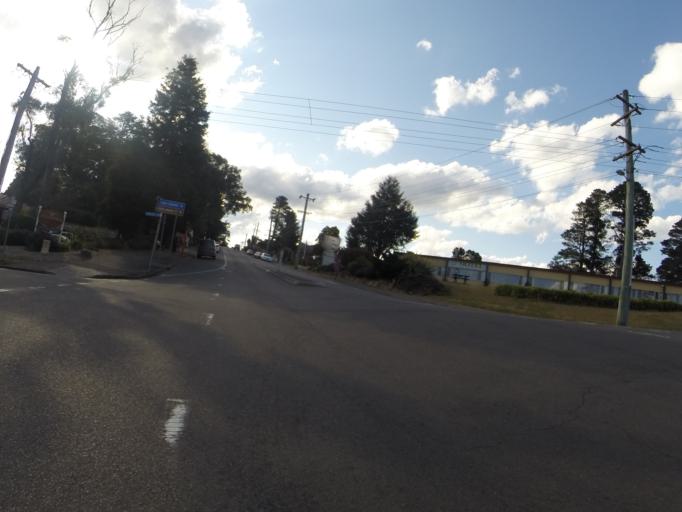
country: AU
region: New South Wales
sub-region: Blue Mountains Municipality
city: Katoomba
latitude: -33.7301
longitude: 150.3118
